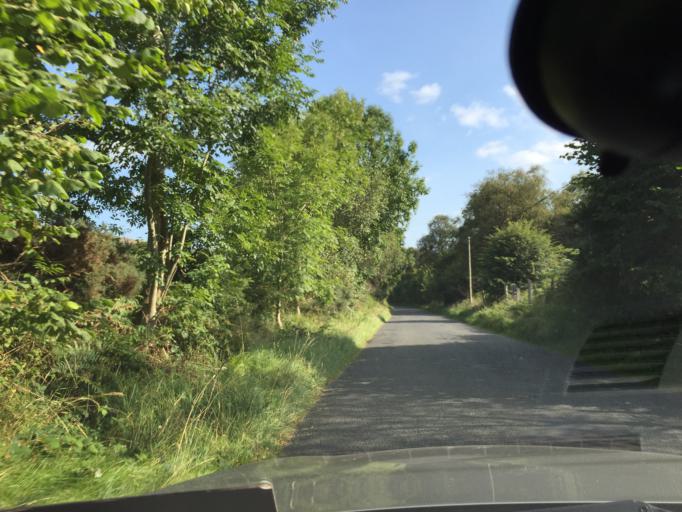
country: IE
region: Leinster
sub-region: Wicklow
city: Rathdrum
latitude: 53.0319
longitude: -6.3128
